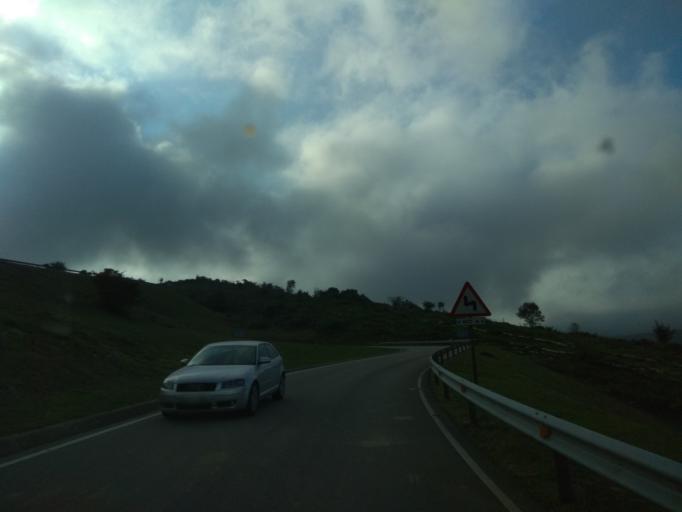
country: ES
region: Cantabria
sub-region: Provincia de Cantabria
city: San Vicente de la Barquera
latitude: 43.3091
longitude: -4.3990
